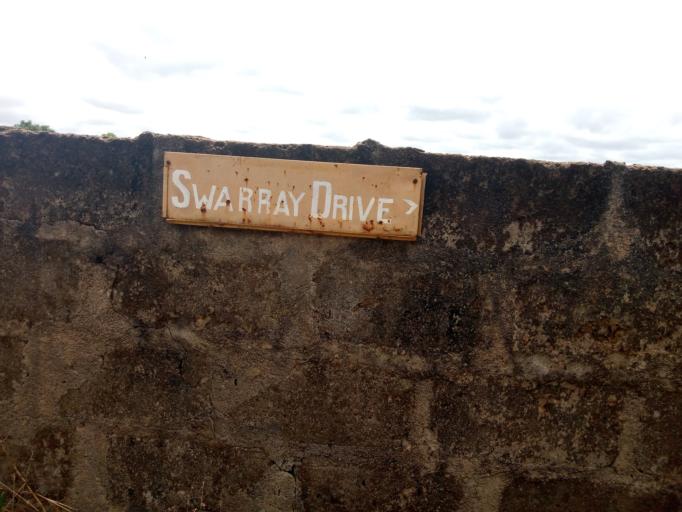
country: SL
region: Western Area
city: Hastings
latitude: 8.4137
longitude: -13.1414
